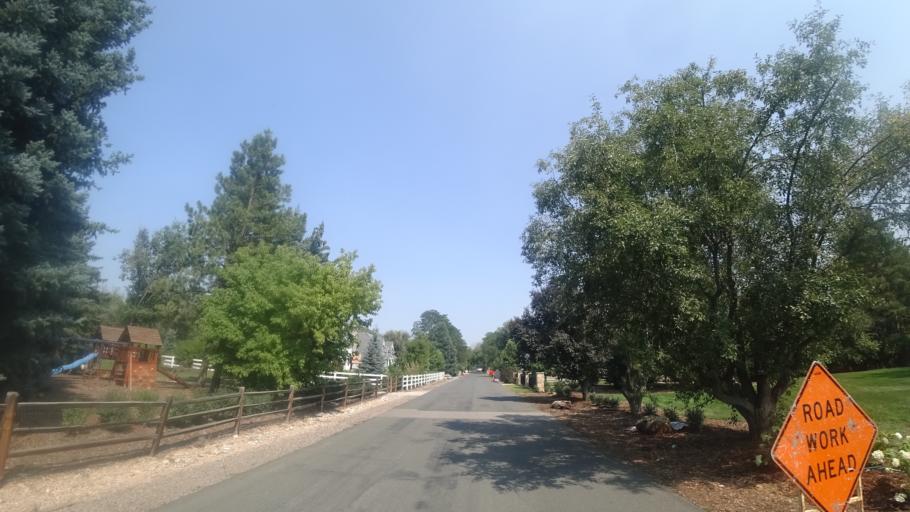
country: US
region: Colorado
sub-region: Arapahoe County
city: Cherry Hills Village
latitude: 39.6295
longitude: -104.9755
